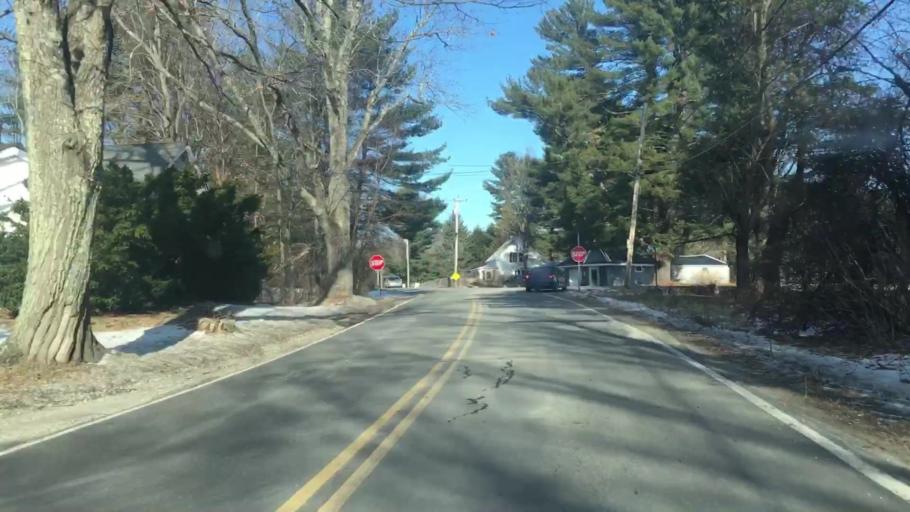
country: US
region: Maine
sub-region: Androscoggin County
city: Auburn
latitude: 44.1188
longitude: -70.2703
